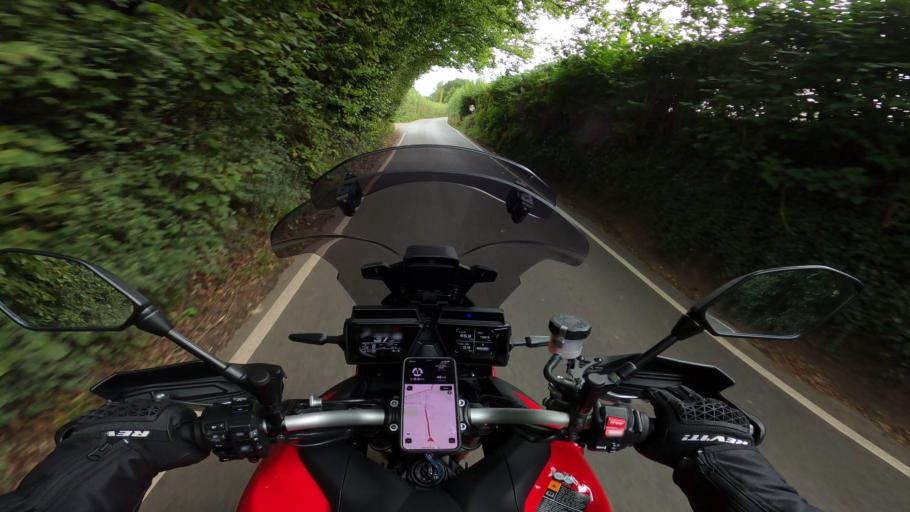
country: GB
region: England
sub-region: Kent
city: Westerham
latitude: 51.2506
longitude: 0.1249
